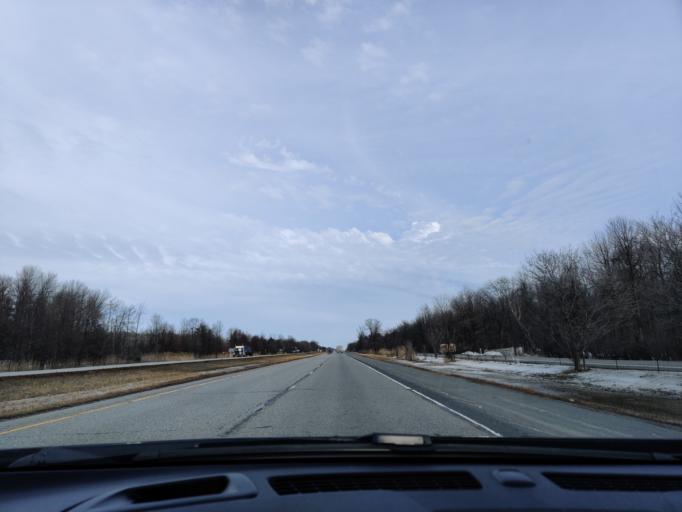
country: CA
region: Quebec
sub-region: Monteregie
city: Les Coteaux
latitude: 45.1491
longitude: -74.4777
